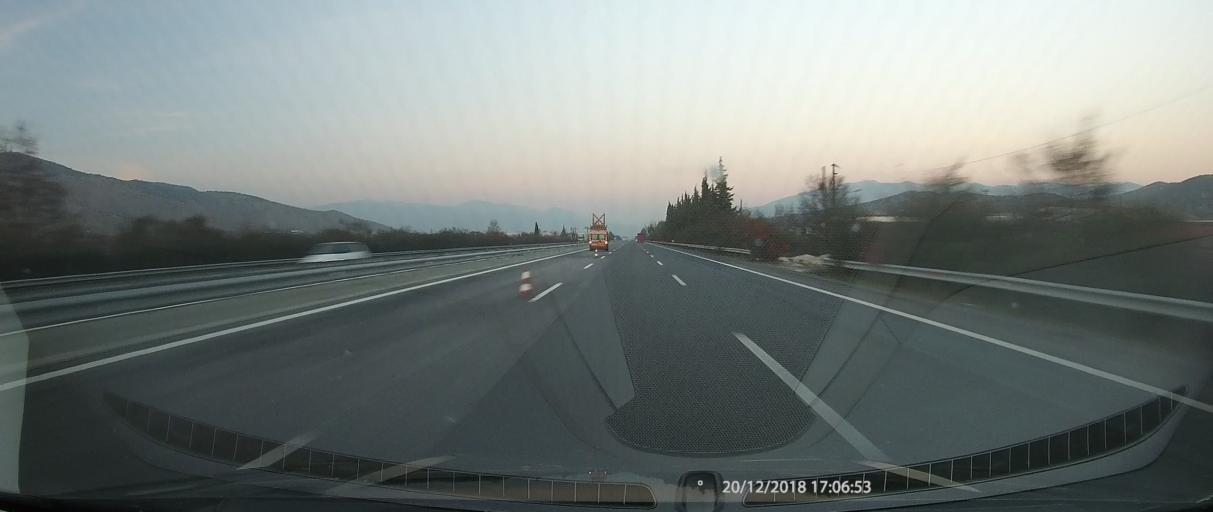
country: GR
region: Thessaly
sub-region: Nomos Larisis
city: Makrychori
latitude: 39.7674
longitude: 22.4826
